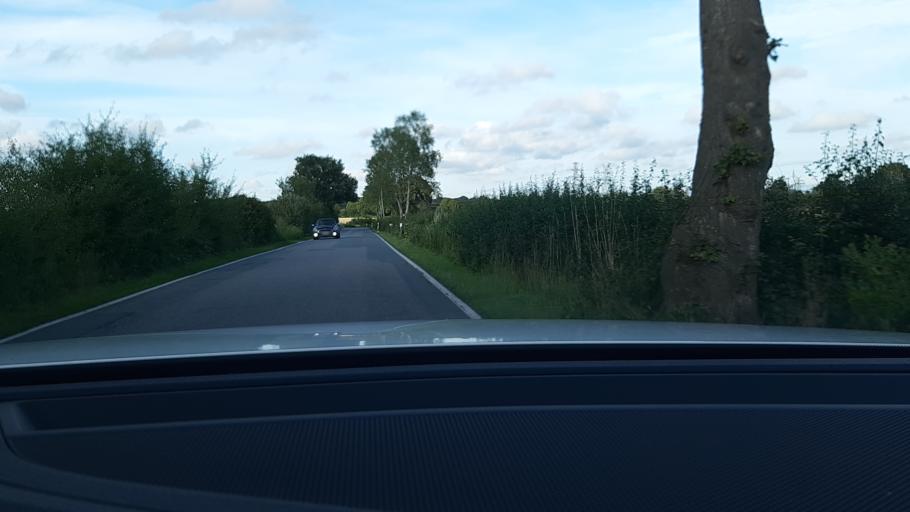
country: DE
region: Schleswig-Holstein
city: Stockelsdorf
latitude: 53.9133
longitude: 10.6339
